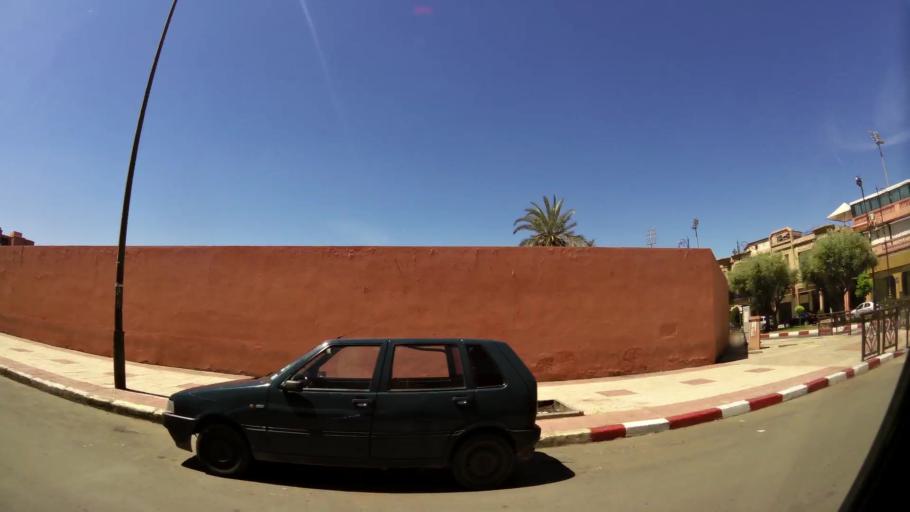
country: MA
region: Marrakech-Tensift-Al Haouz
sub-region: Marrakech
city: Marrakesh
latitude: 31.6273
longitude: -8.0067
